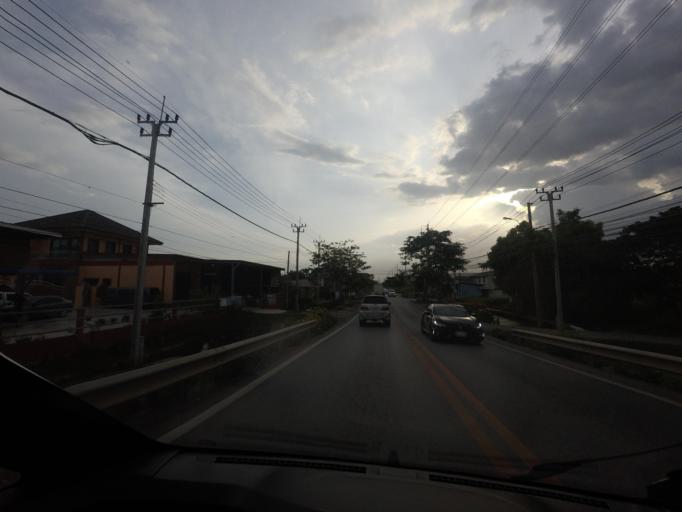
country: TH
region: Bangkok
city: Nong Chok
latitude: 13.8550
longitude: 100.8145
